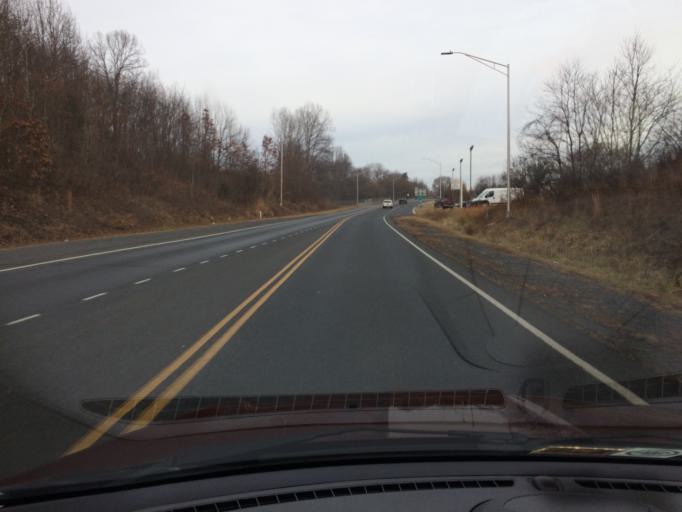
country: US
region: Virginia
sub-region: City of Bedford
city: Bedford
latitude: 37.3438
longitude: -79.5020
